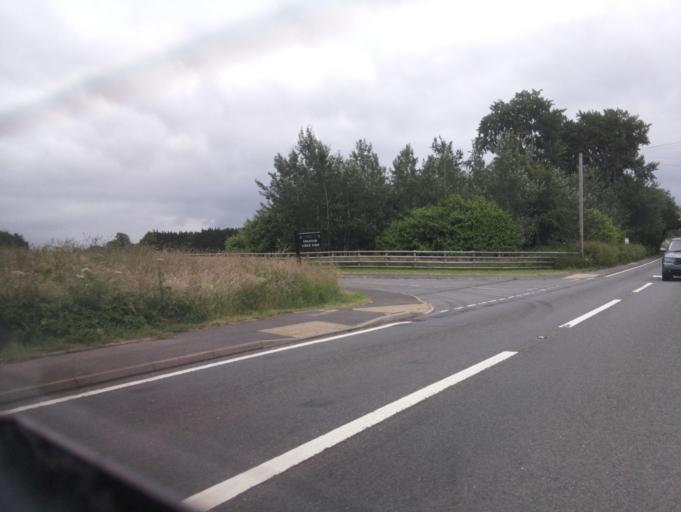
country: GB
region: England
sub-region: Derbyshire
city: Yeldersley
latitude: 52.9794
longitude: -1.6601
